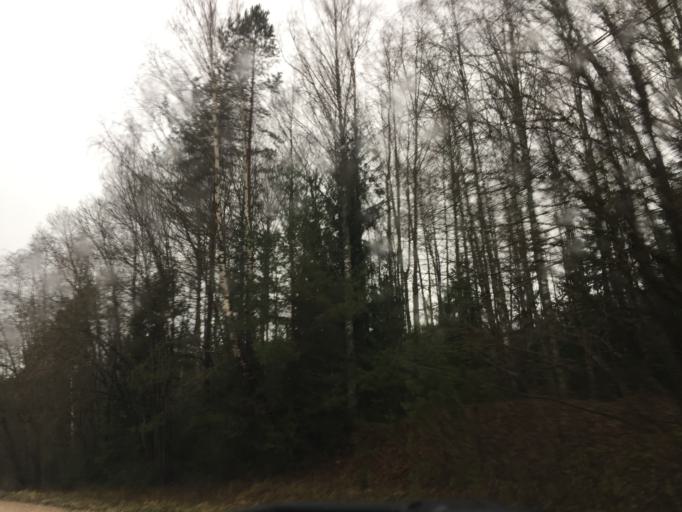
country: LV
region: Salas
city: Sala
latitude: 56.4904
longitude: 25.6378
